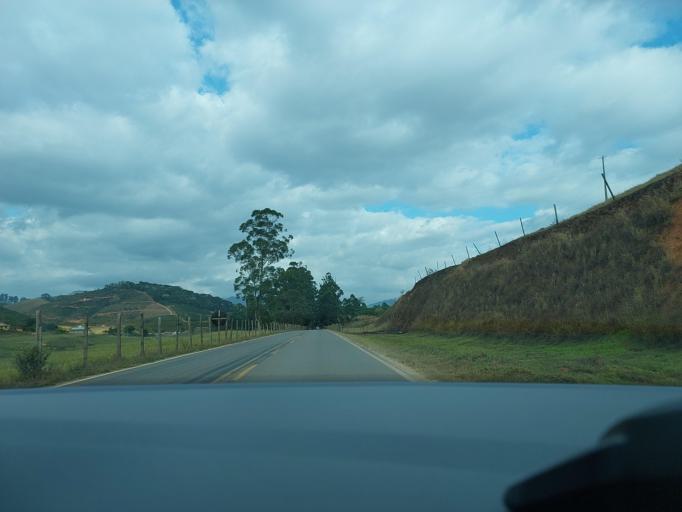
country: BR
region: Minas Gerais
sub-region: Visconde Do Rio Branco
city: Visconde do Rio Branco
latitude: -20.9038
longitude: -42.6508
